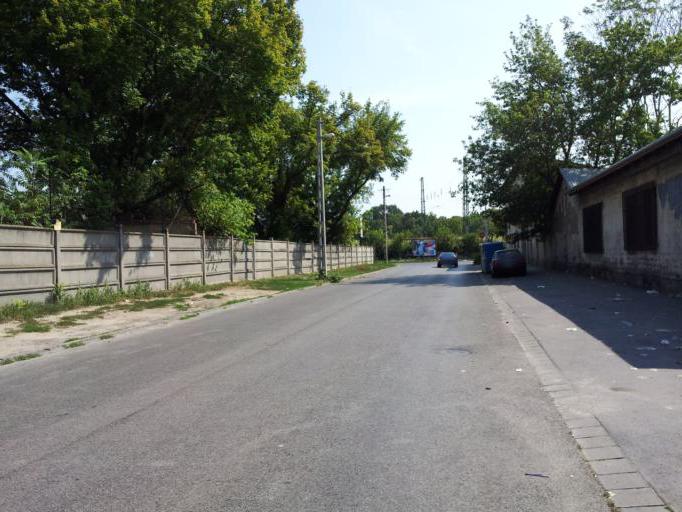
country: HU
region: Budapest
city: Budapest XIV. keruelet
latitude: 47.4972
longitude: 19.1149
